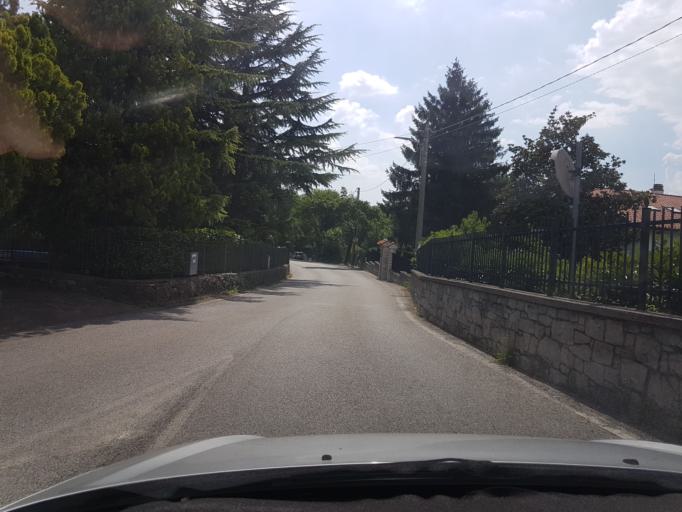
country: IT
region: Friuli Venezia Giulia
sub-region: Provincia di Trieste
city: Zolla
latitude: 45.7228
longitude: 13.7895
